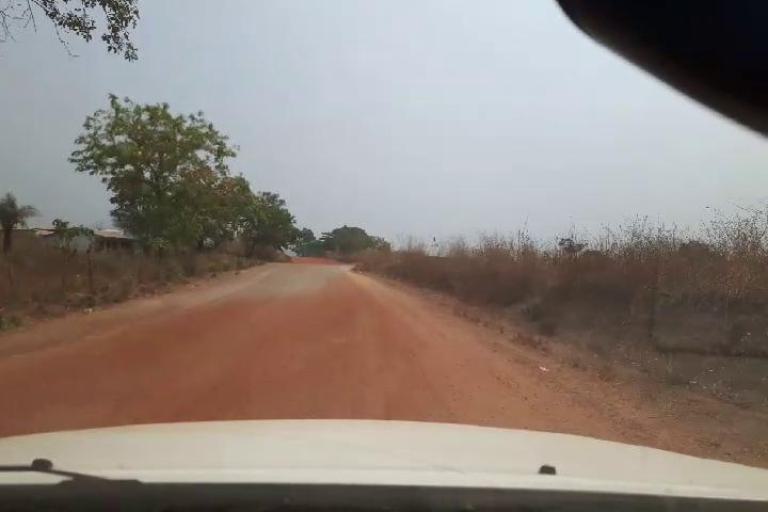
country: SL
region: Northern Province
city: Bumbuna
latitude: 9.0043
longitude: -11.7742
